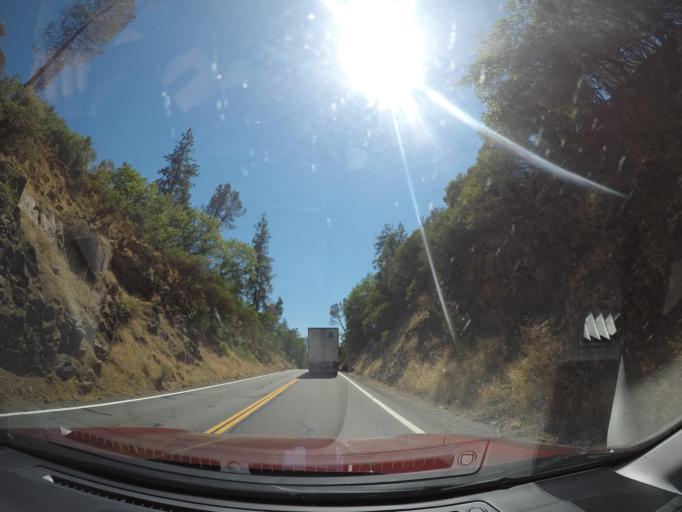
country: US
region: California
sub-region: Shasta County
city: Bella Vista
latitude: 40.7058
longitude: -122.0929
